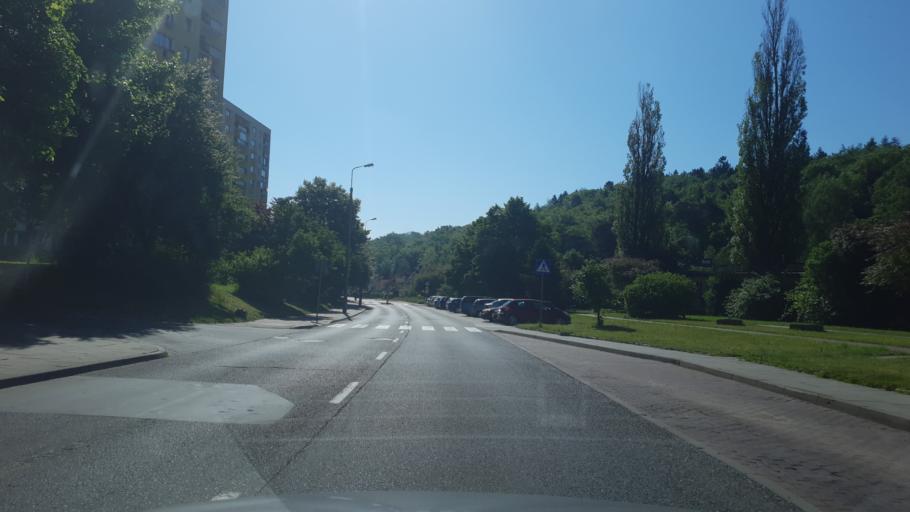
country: PL
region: Pomeranian Voivodeship
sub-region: Sopot
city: Sopot
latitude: 54.4565
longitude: 18.5394
